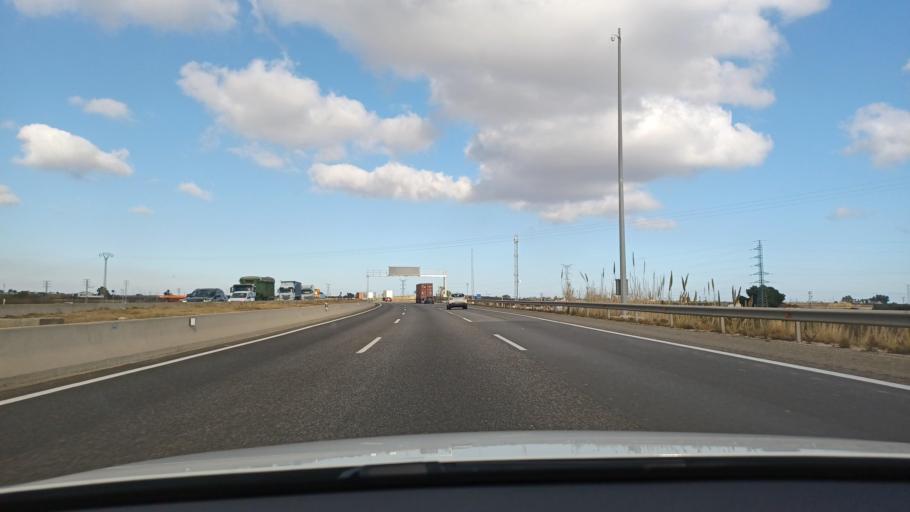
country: ES
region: Valencia
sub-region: Provincia de Valencia
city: Alginet
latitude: 39.2572
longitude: -0.4627
